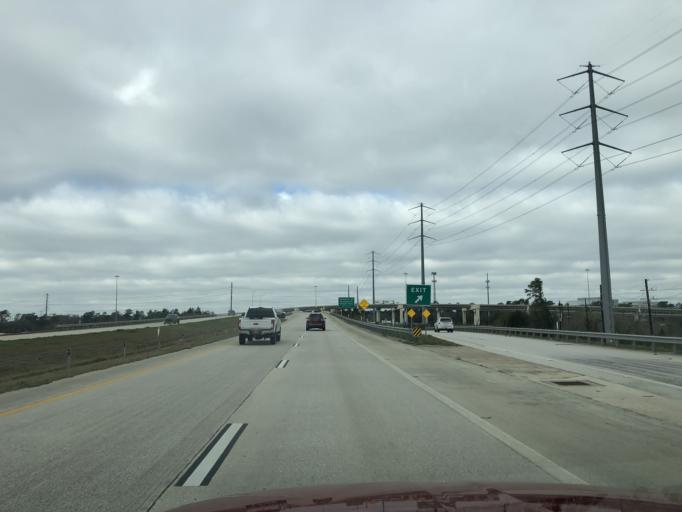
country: US
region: Texas
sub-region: Harris County
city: Spring
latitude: 30.0922
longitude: -95.4289
